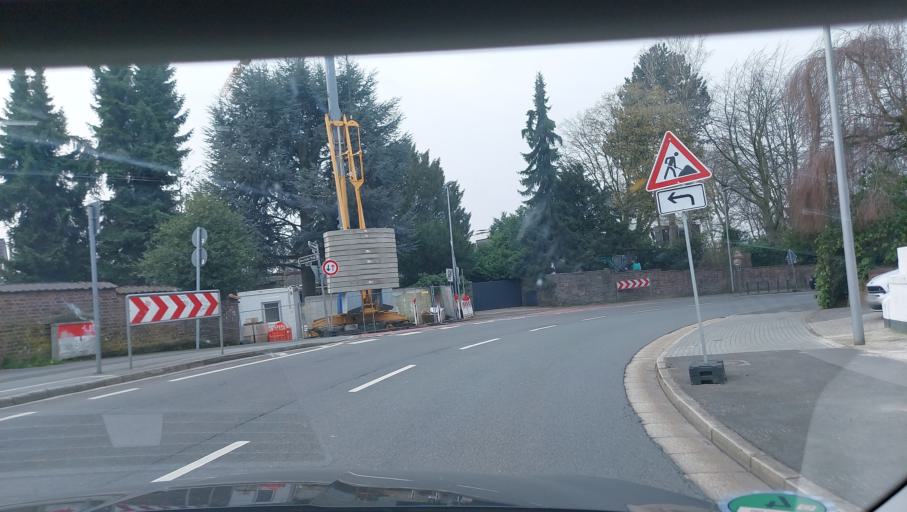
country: DE
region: North Rhine-Westphalia
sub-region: Regierungsbezirk Dusseldorf
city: Erkrath
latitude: 51.2471
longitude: 6.8631
